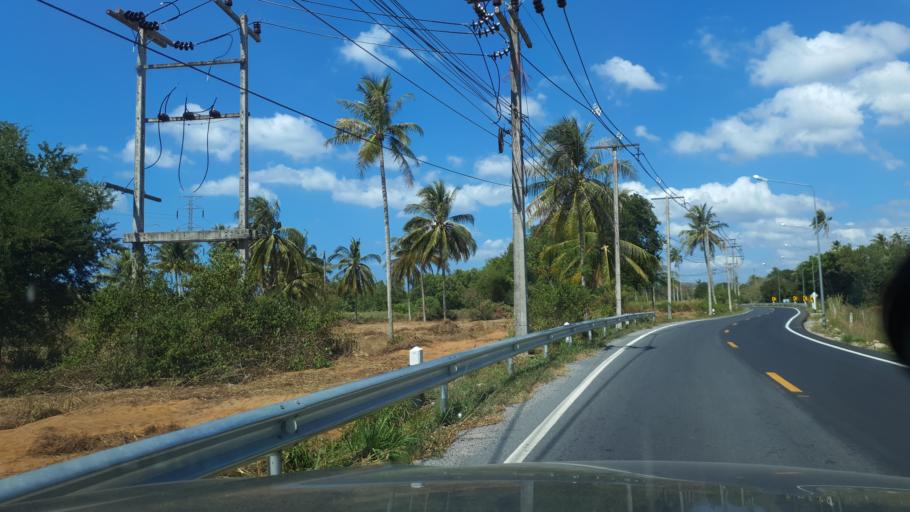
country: TH
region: Phuket
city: Thalang
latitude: 8.1535
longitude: 98.3051
